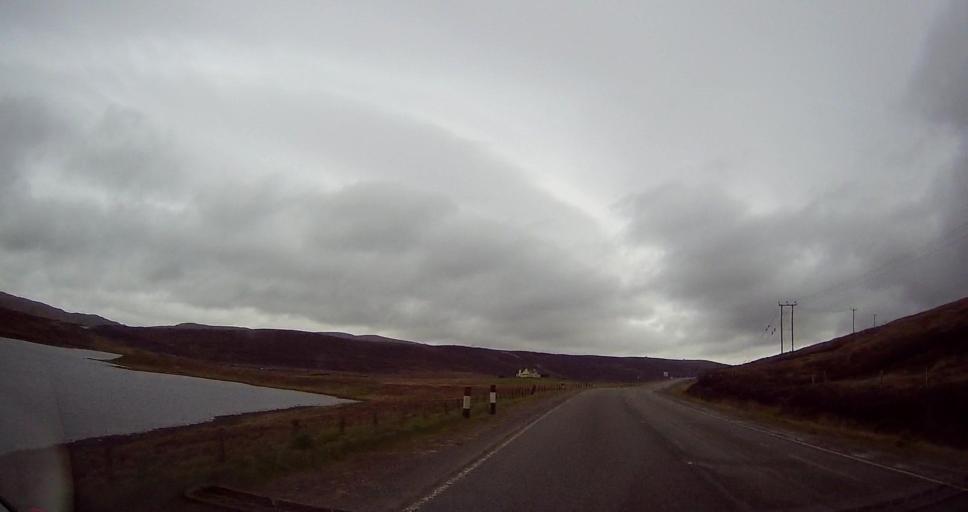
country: GB
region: Scotland
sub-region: Shetland Islands
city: Lerwick
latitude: 60.2744
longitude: -1.2420
